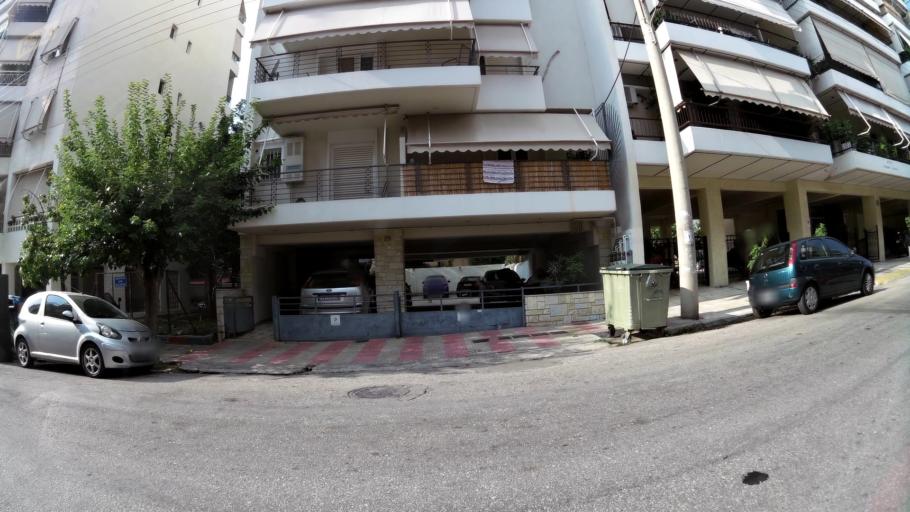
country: GR
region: Attica
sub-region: Nomarchia Athinas
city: Dhafni
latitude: 37.9426
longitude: 23.7262
